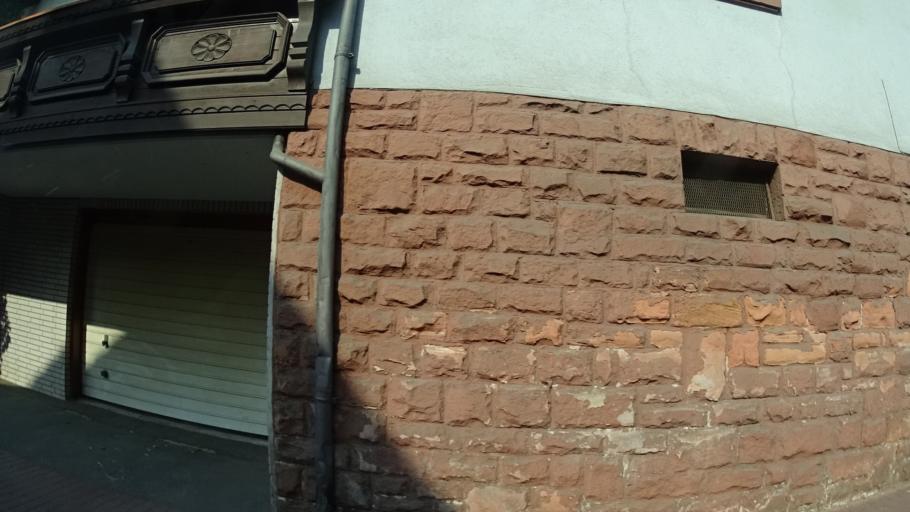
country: DE
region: Bavaria
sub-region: Regierungsbezirk Unterfranken
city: Heimbuchenthal
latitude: 49.8822
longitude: 9.2935
